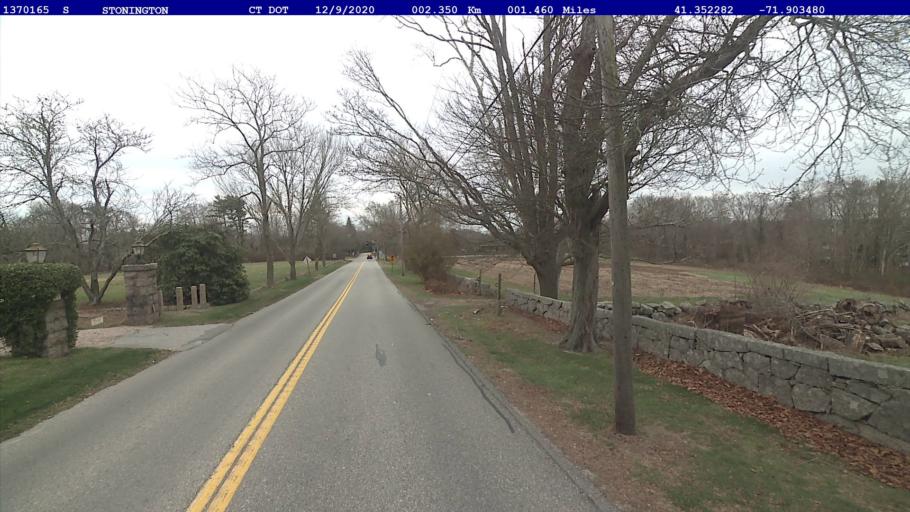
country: US
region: Connecticut
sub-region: New London County
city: Mystic
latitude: 41.3523
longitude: -71.9035
